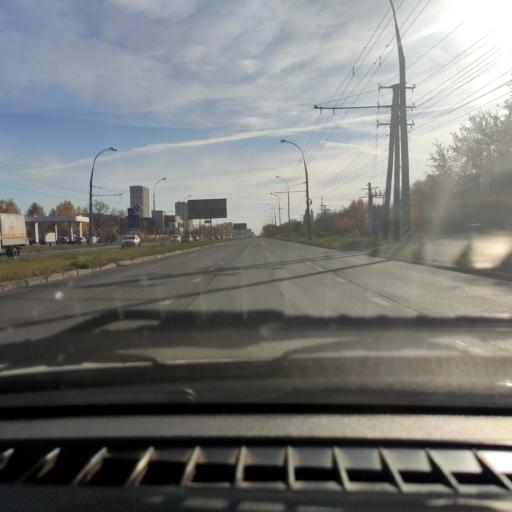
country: RU
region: Samara
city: Tol'yatti
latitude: 53.5479
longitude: 49.3019
